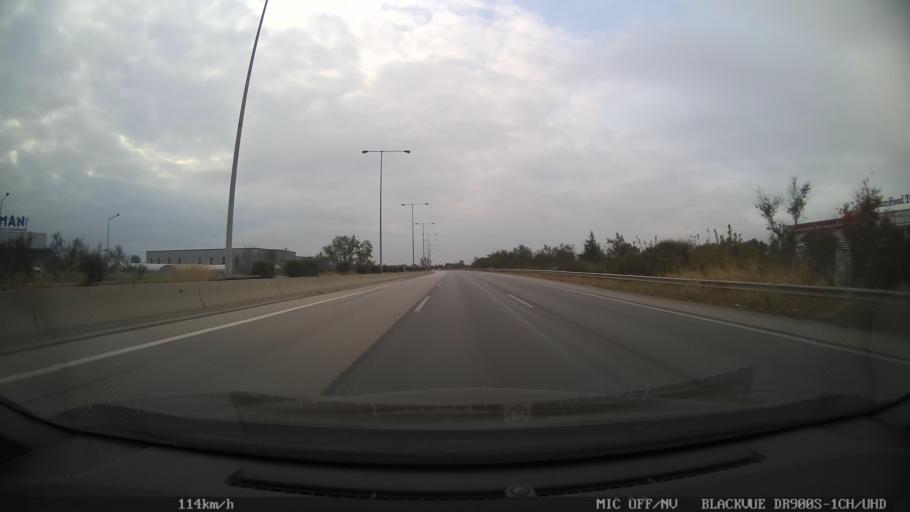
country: GR
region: Central Macedonia
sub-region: Nomos Thessalonikis
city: Nea Magnisia
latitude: 40.6777
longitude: 22.8323
